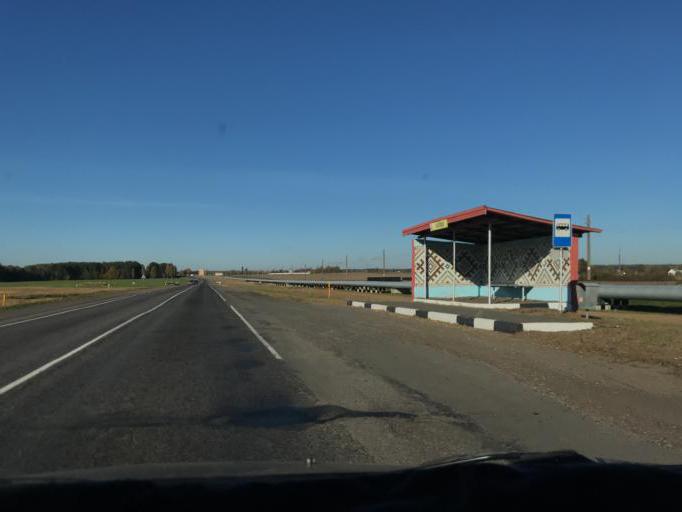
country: BY
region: Gomel
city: Mazyr
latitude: 51.9870
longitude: 29.2595
